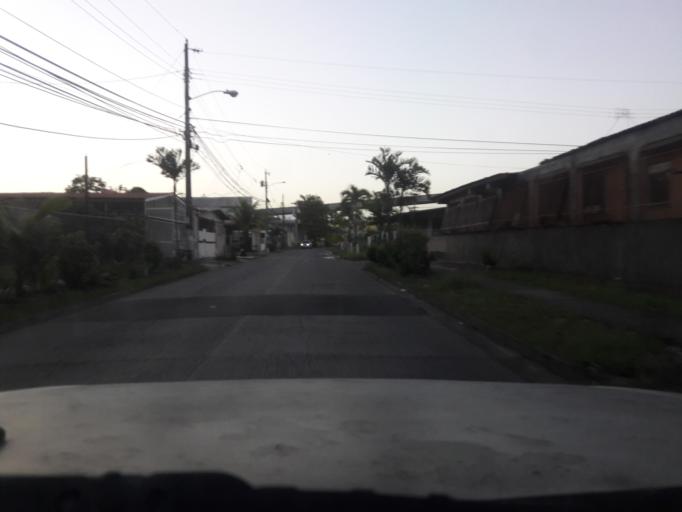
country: PA
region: Panama
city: San Miguelito
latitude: 9.0540
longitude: -79.4374
